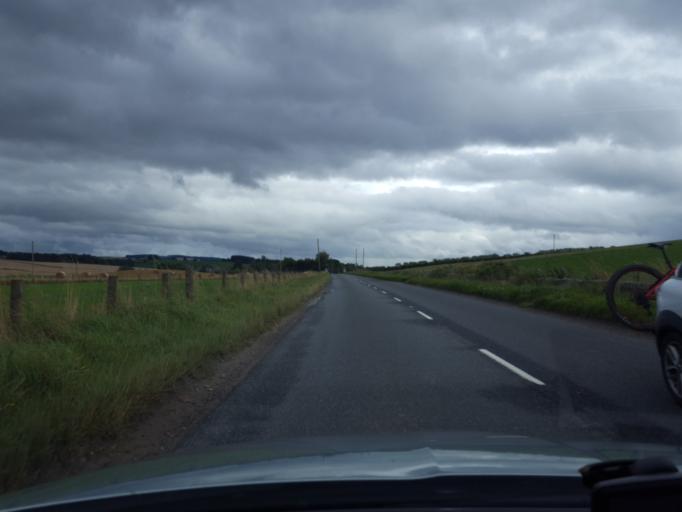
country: GB
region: Scotland
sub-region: Aberdeenshire
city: Kemnay
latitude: 57.1747
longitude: -2.4275
